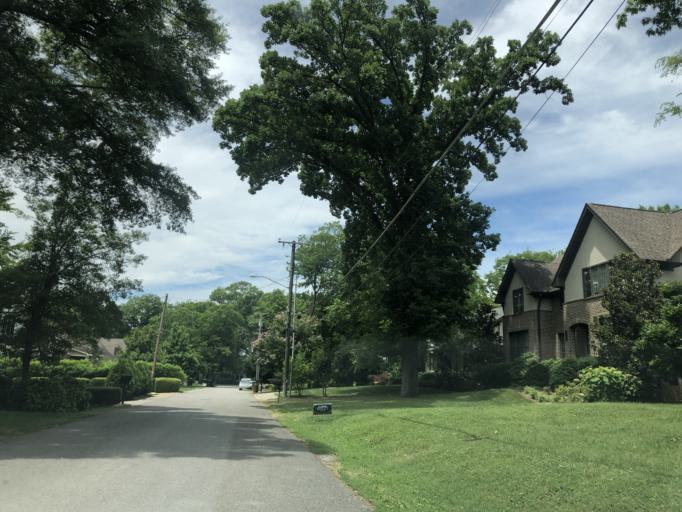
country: US
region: Tennessee
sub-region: Davidson County
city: Oak Hill
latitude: 36.1026
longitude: -86.8039
